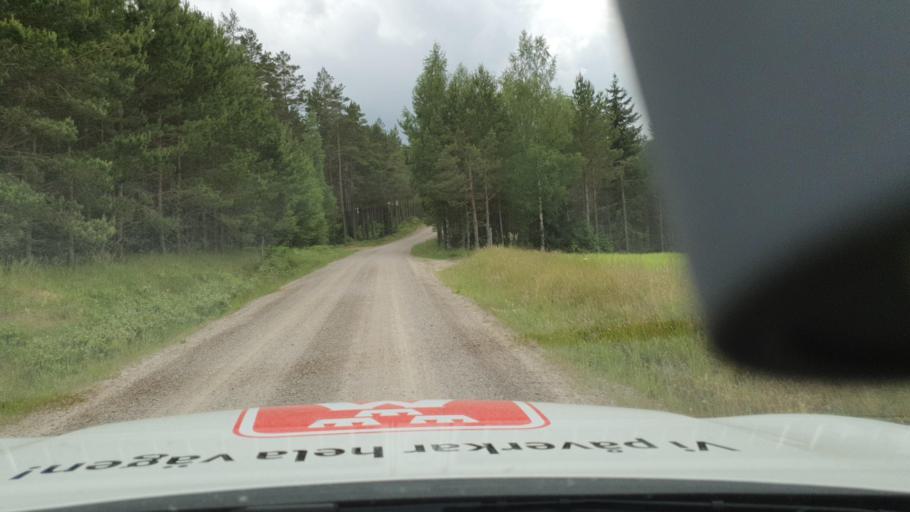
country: SE
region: Vaestra Goetaland
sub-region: Tidaholms Kommun
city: Olofstorp
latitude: 58.2117
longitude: 14.1096
